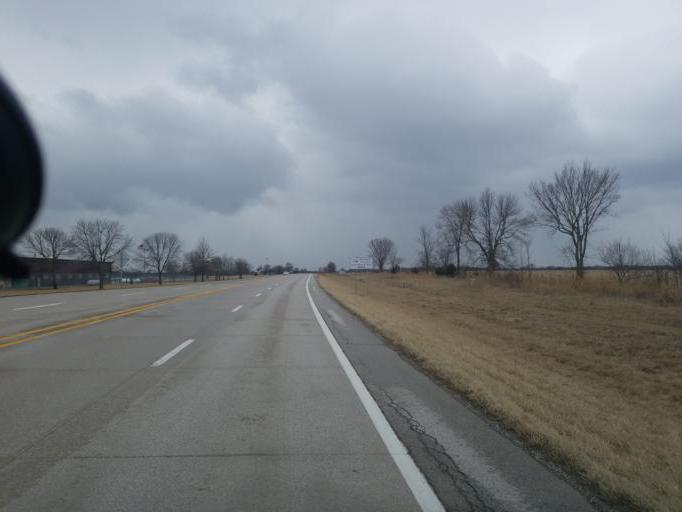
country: US
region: Missouri
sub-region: Macon County
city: Macon
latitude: 39.7979
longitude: -92.4758
